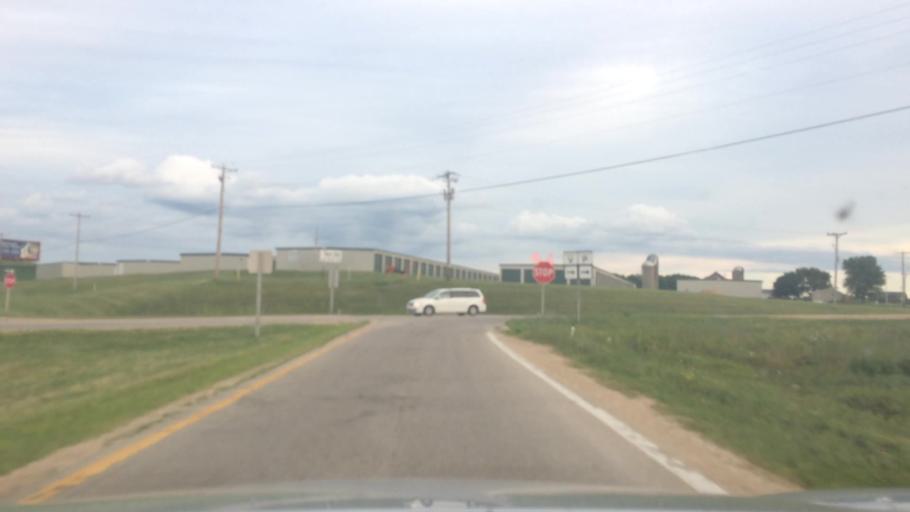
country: US
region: Wisconsin
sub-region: Columbia County
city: Lodi
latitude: 43.2520
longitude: -89.5203
